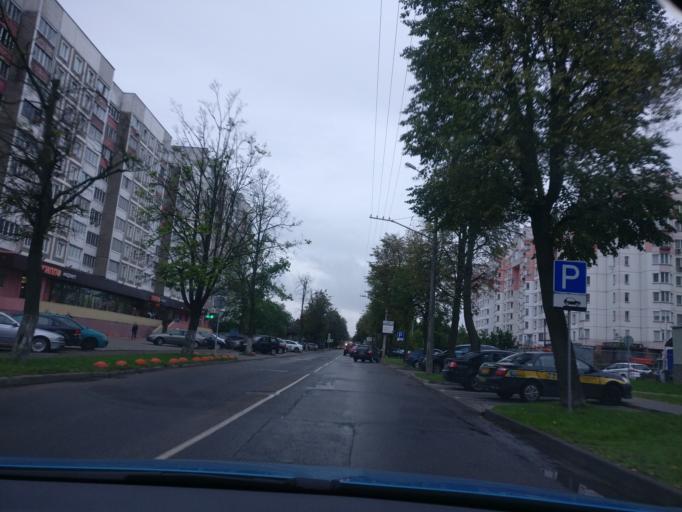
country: BY
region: Minsk
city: Minsk
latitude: 53.9296
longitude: 27.5485
